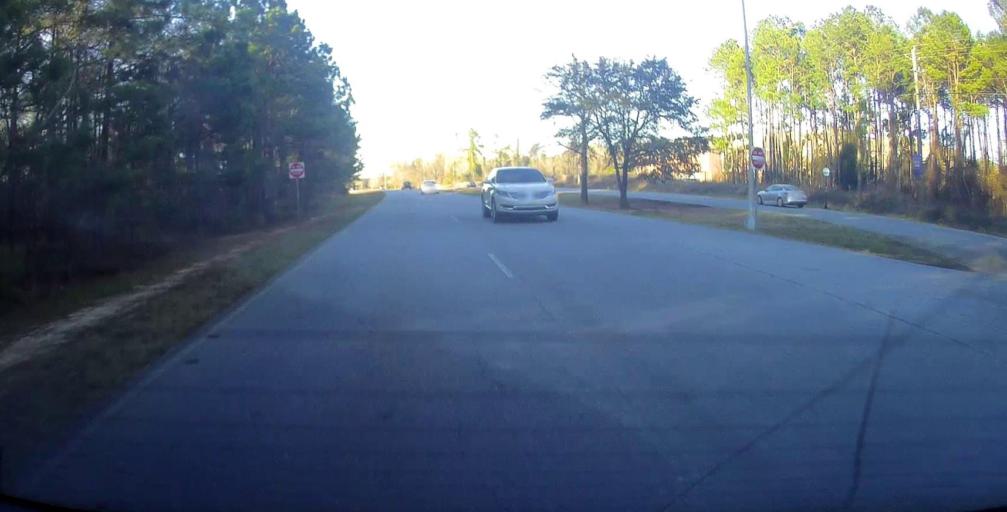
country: US
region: Georgia
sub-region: Dougherty County
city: Albany
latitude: 31.5773
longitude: -84.2197
